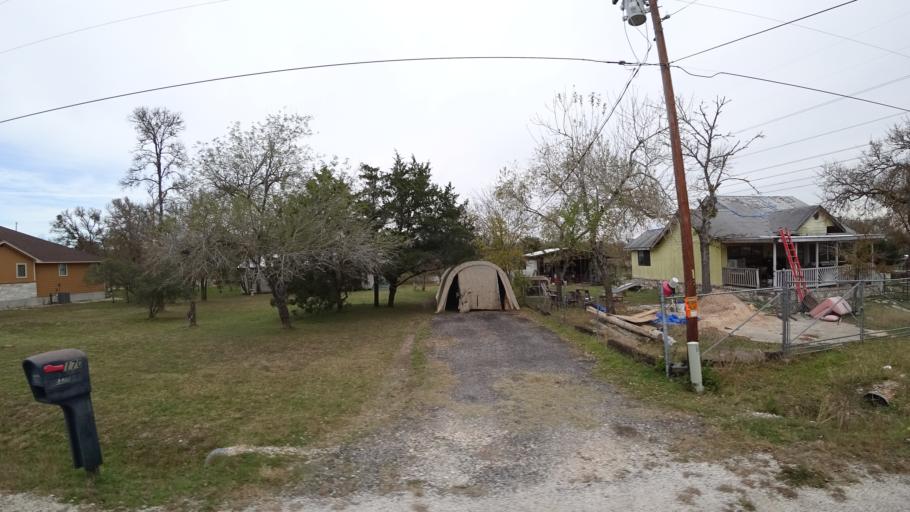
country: US
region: Texas
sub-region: Travis County
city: Garfield
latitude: 30.1003
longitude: -97.5706
